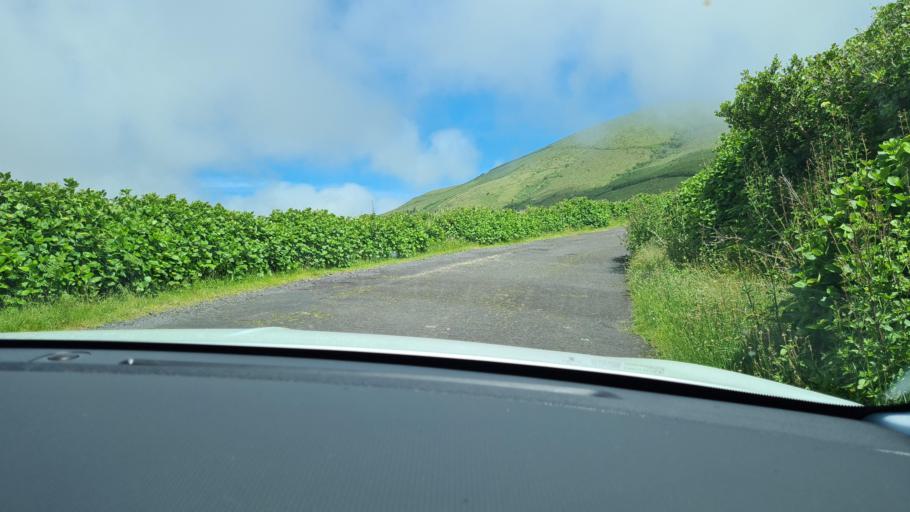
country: PT
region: Azores
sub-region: Sao Roque do Pico
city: Sao Roque do Pico
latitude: 38.6710
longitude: -28.1334
